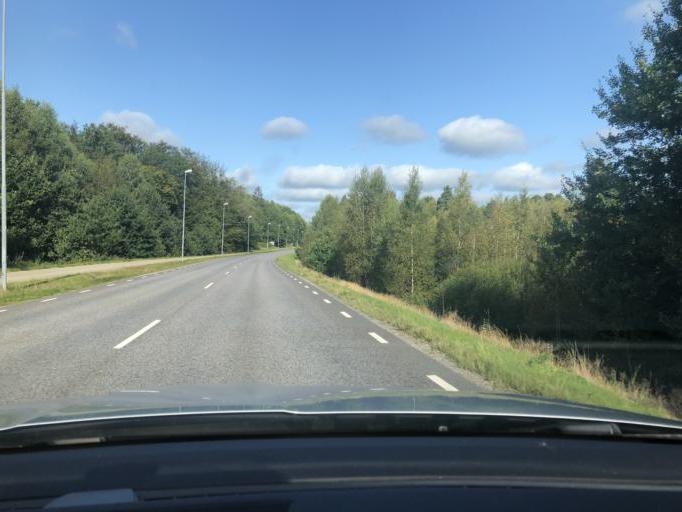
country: SE
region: Blekinge
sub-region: Olofstroms Kommun
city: Olofstroem
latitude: 56.2626
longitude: 14.5530
